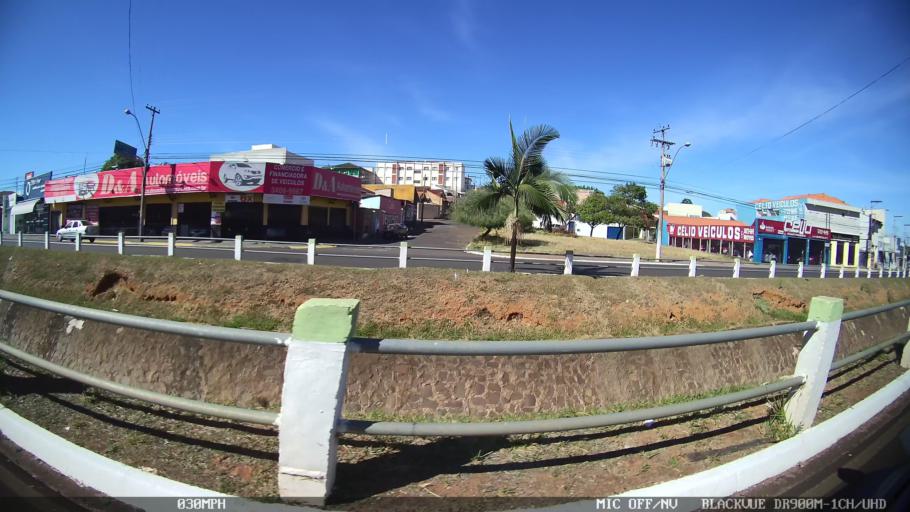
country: BR
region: Sao Paulo
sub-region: Franca
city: Franca
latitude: -20.5207
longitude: -47.3988
